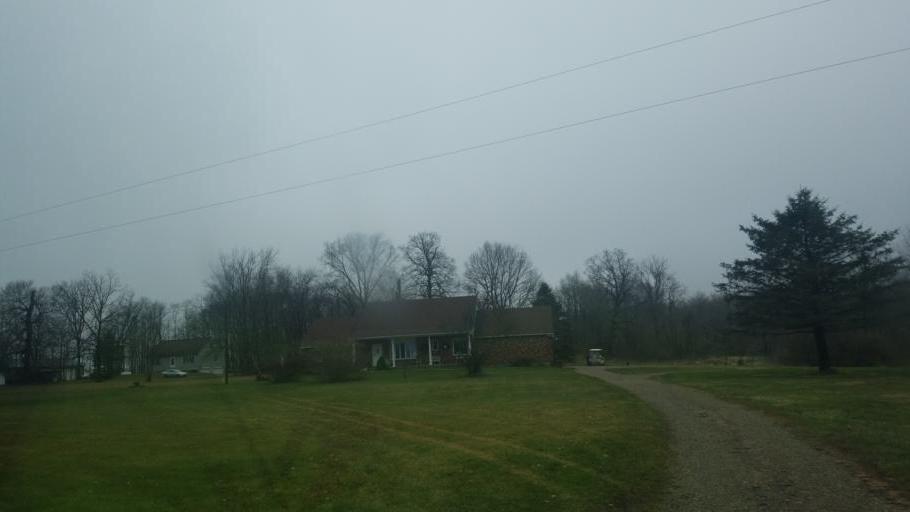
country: US
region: Ohio
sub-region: Champaign County
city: North Lewisburg
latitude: 40.2452
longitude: -83.5409
